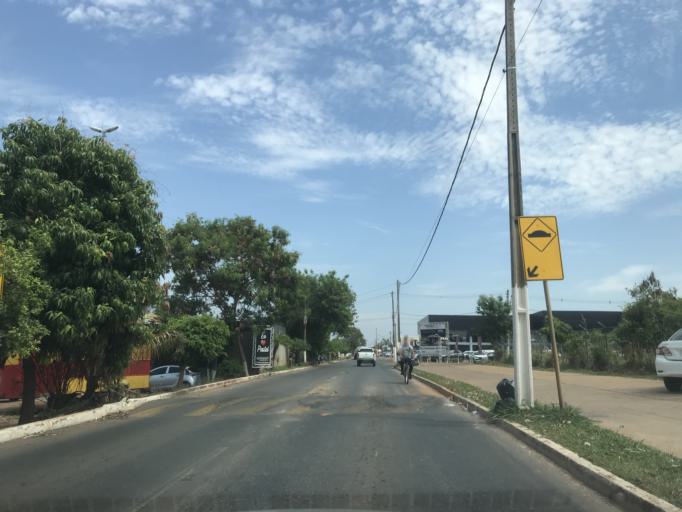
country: BR
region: Federal District
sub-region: Brasilia
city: Brasilia
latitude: -15.7919
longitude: -47.9709
